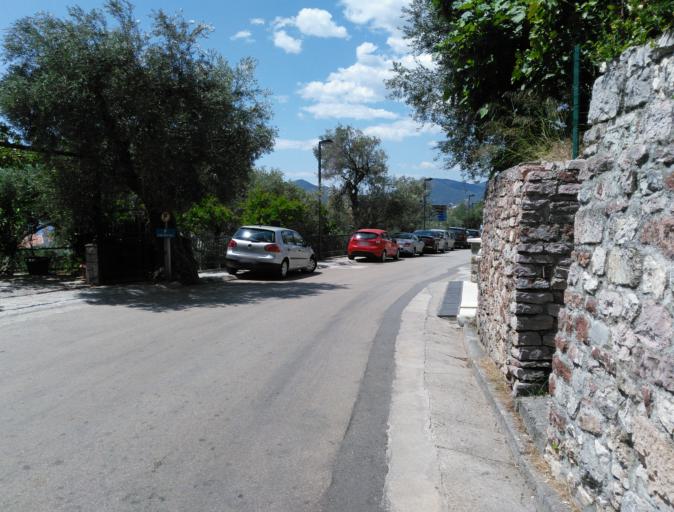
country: ME
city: Petrovac na Moru
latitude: 42.2547
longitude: 18.8984
